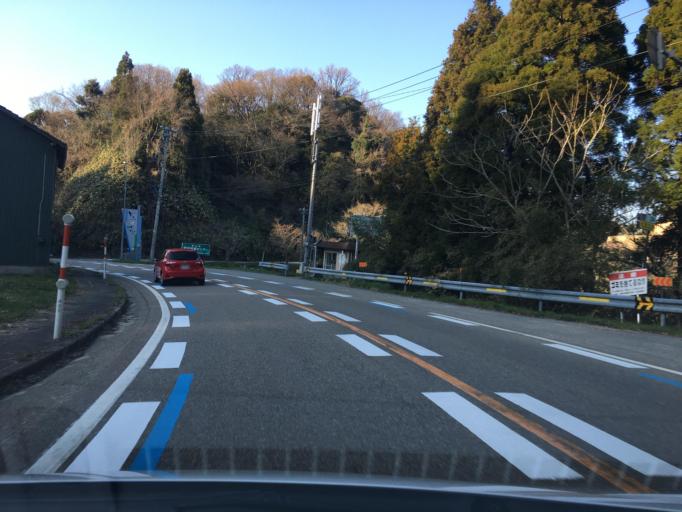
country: JP
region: Toyama
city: Himi
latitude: 36.9263
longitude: 137.0264
